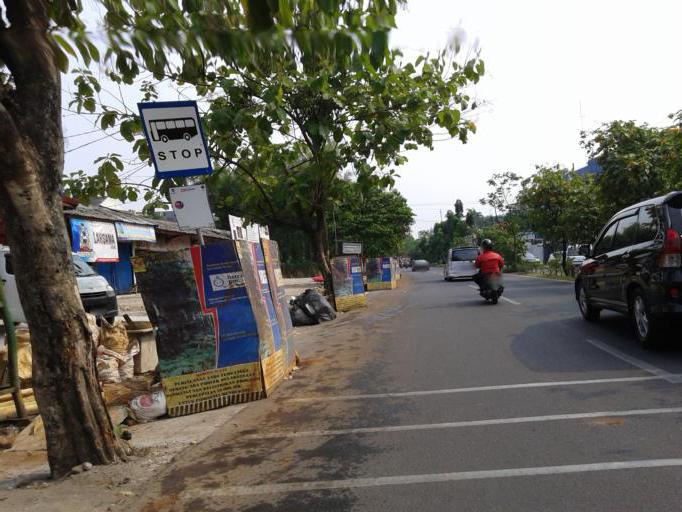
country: ID
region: West Java
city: Pamulang
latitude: -6.3069
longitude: 106.7817
